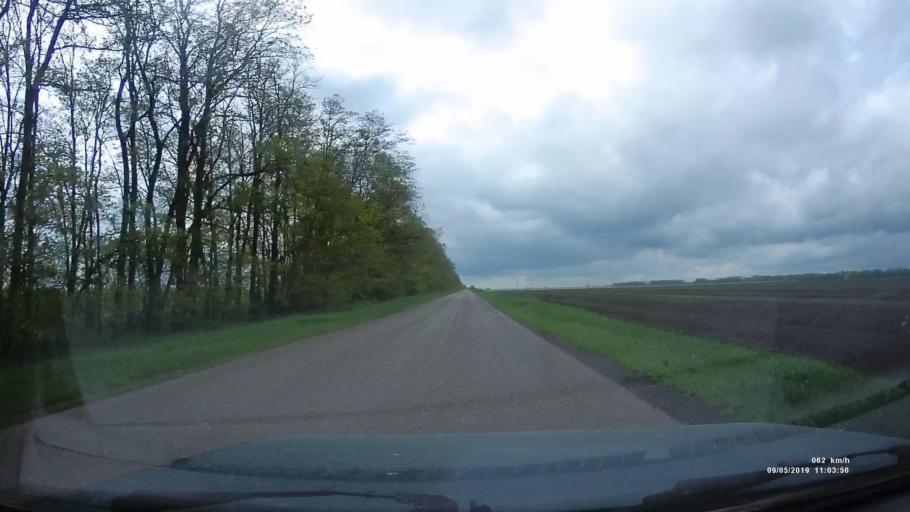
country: RU
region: Krasnodarskiy
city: Kanelovskaya
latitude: 46.8239
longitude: 39.2101
